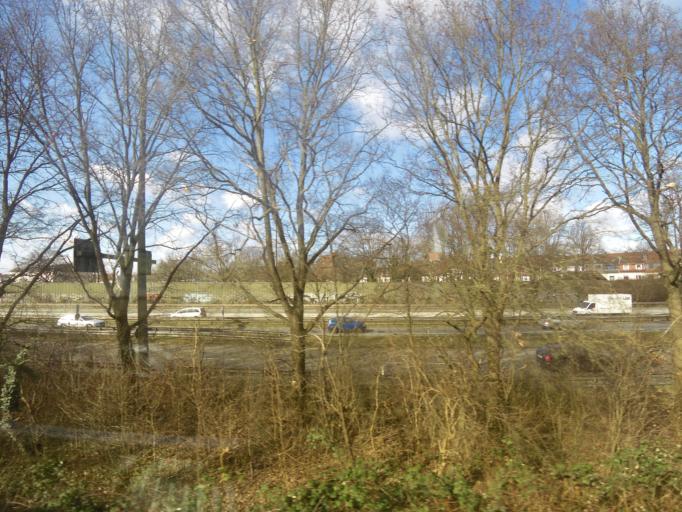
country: DE
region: Bremen
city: Bremen
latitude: 53.0992
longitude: 8.7965
